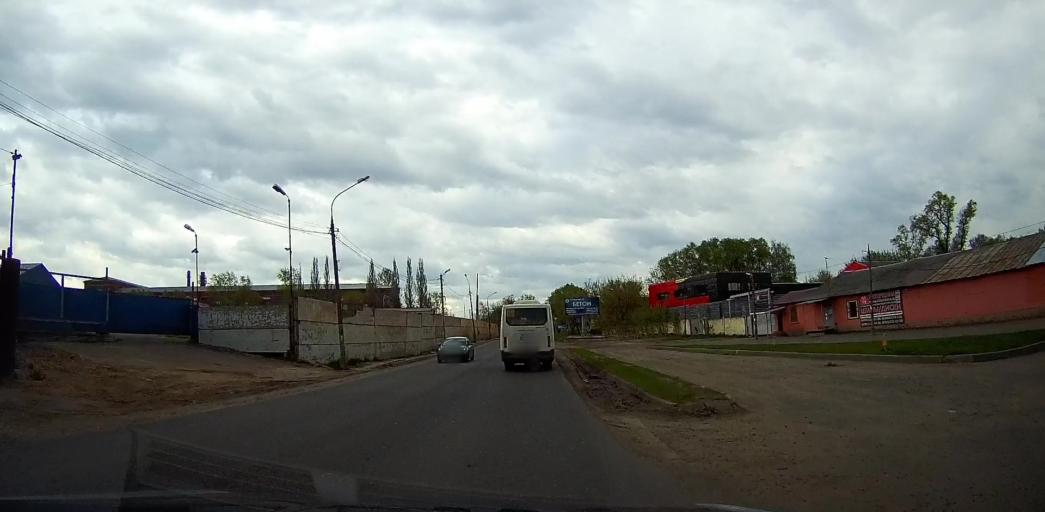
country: RU
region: Moskovskaya
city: Pavlovskiy Posad
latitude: 55.7789
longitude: 38.6874
